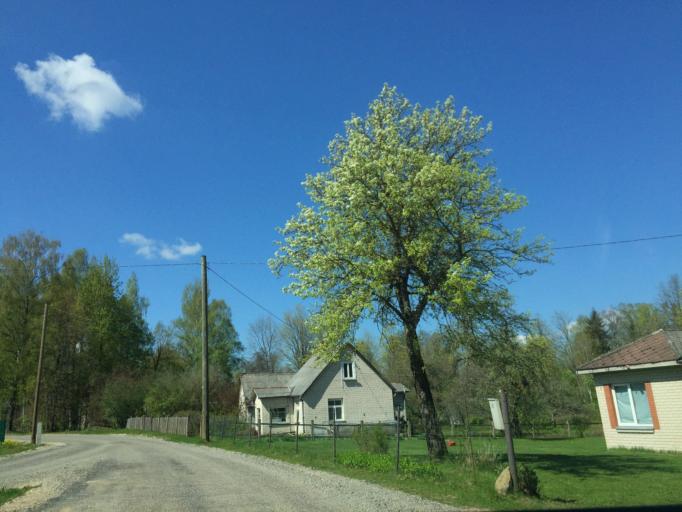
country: LV
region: Baldone
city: Baldone
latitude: 56.7410
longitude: 24.3735
